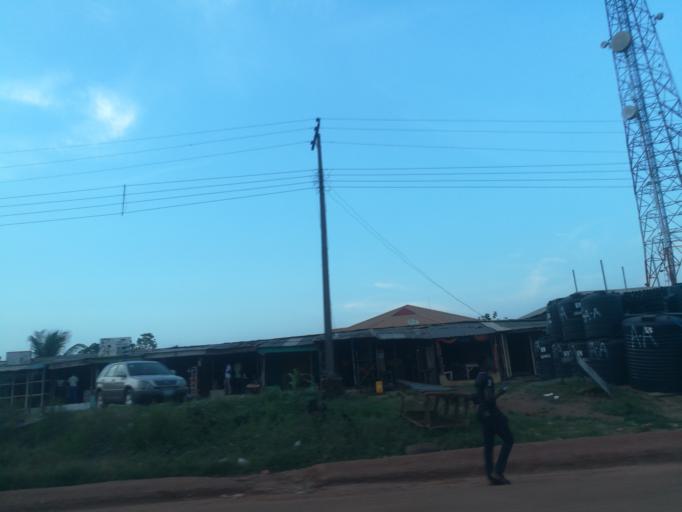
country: NG
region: Ogun
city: Abeokuta
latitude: 7.1776
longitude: 3.3920
